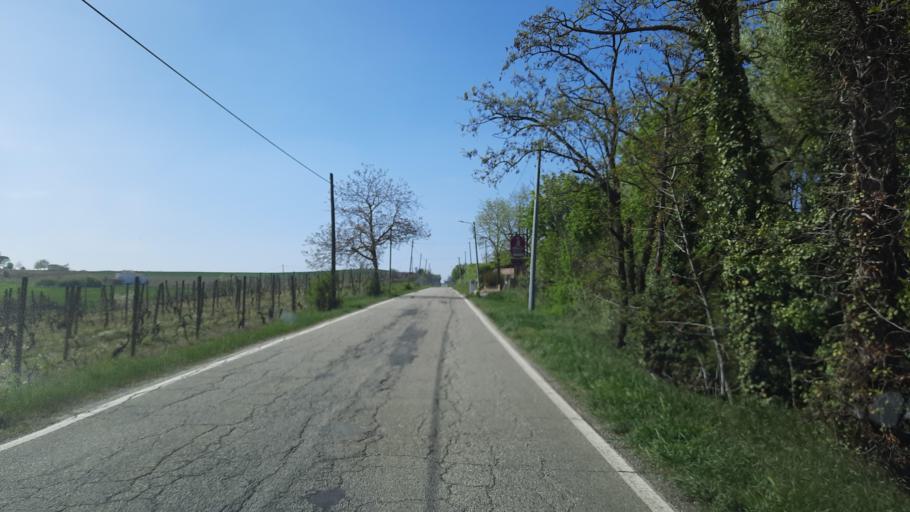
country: IT
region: Piedmont
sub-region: Provincia di Alessandria
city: Altavilla Monferrato
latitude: 45.0124
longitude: 8.3734
